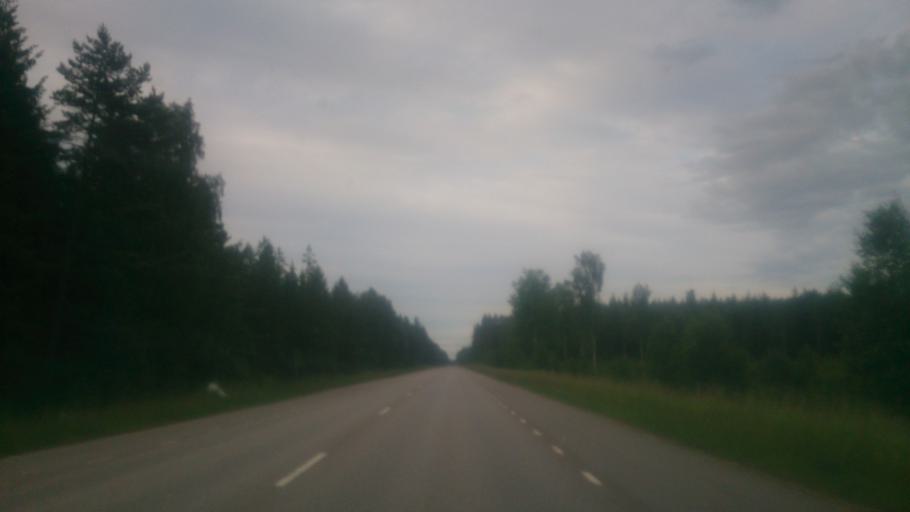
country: SE
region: OEstergoetland
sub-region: Motala Kommun
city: Borensberg
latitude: 58.4865
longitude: 15.2862
